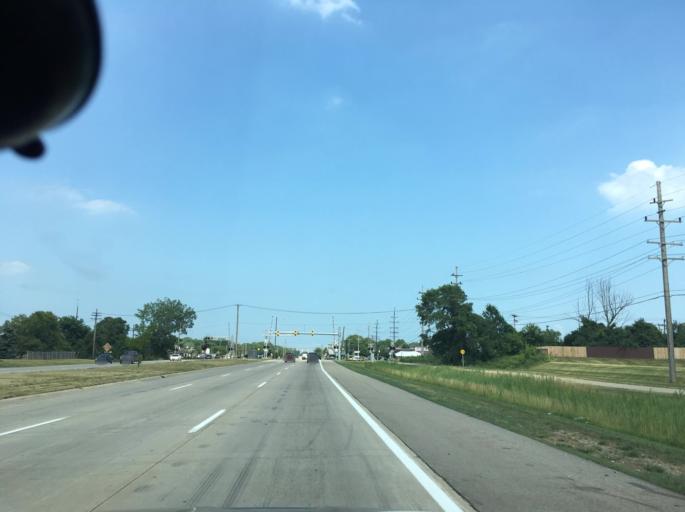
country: US
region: Michigan
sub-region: Macomb County
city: Clinton
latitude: 42.5690
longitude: -82.9170
